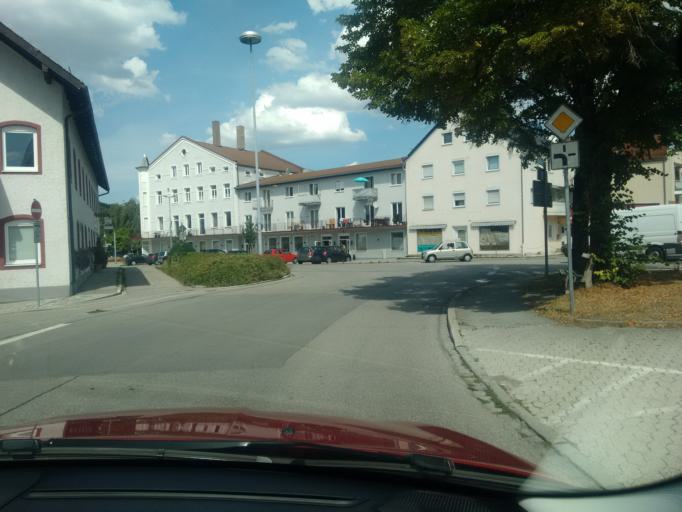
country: DE
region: Bavaria
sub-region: Upper Bavaria
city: Trostberg an der Alz
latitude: 48.0255
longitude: 12.5550
